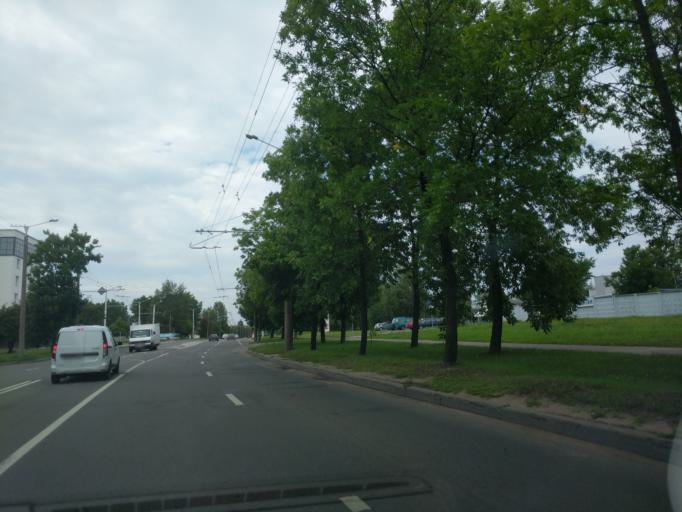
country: BY
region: Minsk
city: Novoye Medvezhino
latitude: 53.8838
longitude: 27.4818
